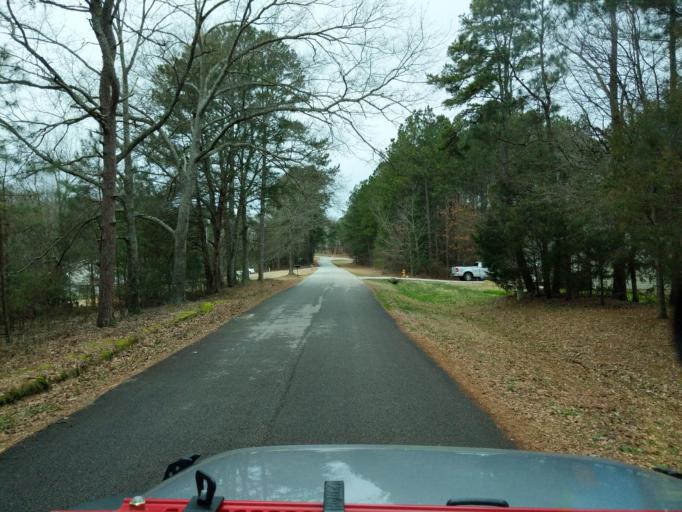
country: US
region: Georgia
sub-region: Franklin County
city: Gumlog
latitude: 34.4750
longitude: -83.0371
